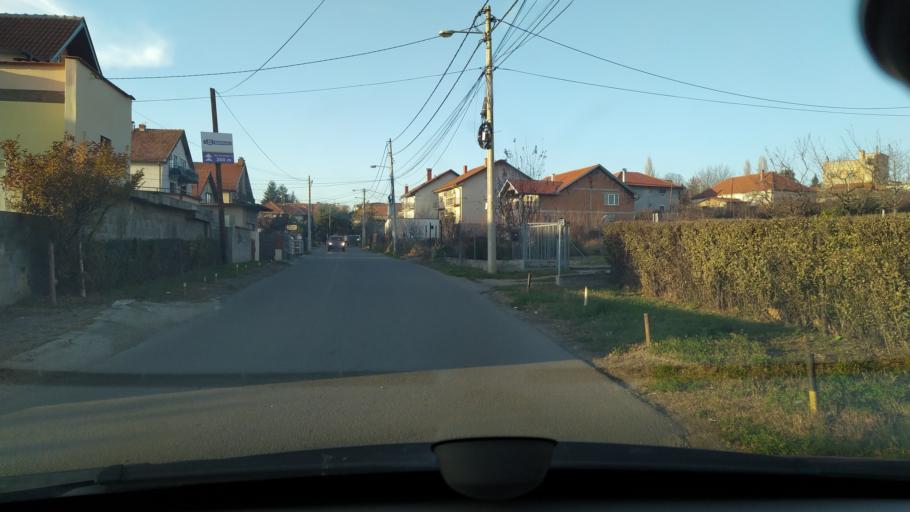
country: RS
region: Central Serbia
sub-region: Belgrade
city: Zvezdara
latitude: 44.7631
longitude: 20.5626
